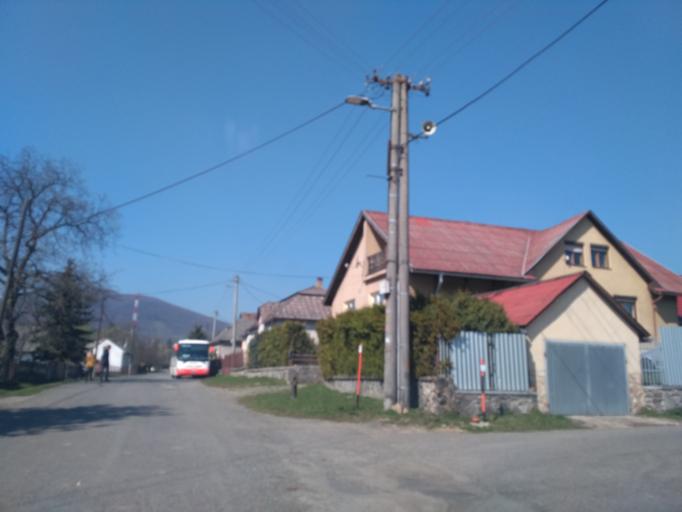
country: SK
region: Presovsky
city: Vranov nad Topl'ou
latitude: 48.8050
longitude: 21.6399
